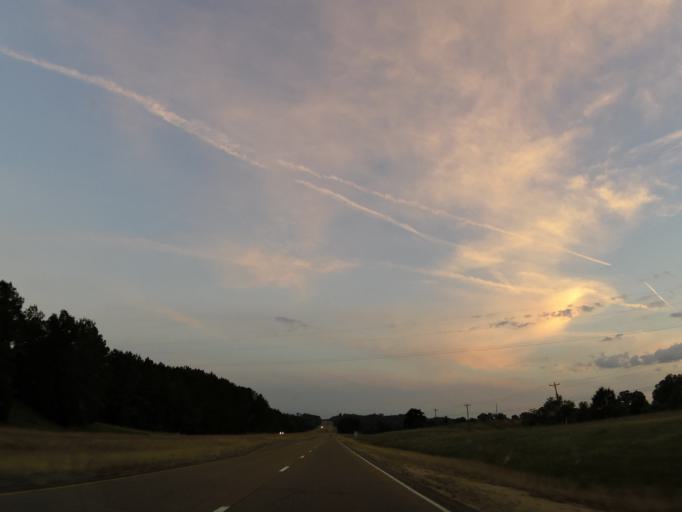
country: US
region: Mississippi
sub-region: Lauderdale County
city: Meridian Station
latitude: 32.6569
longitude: -88.4938
